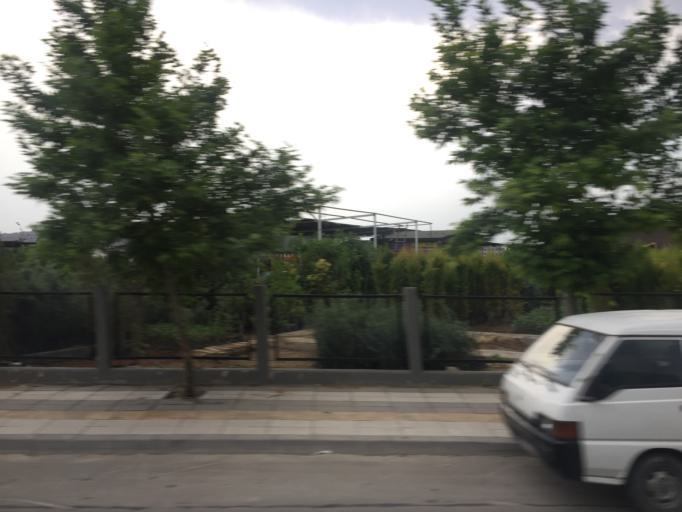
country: TR
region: Gaziantep
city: Gaziantep
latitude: 37.0600
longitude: 37.4156
